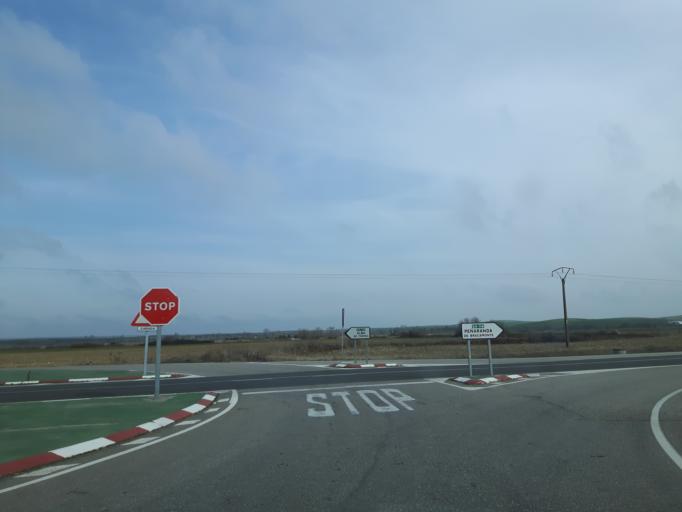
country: ES
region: Castille and Leon
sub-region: Provincia de Salamanca
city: Coca de Alba
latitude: 40.8715
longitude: -5.3772
